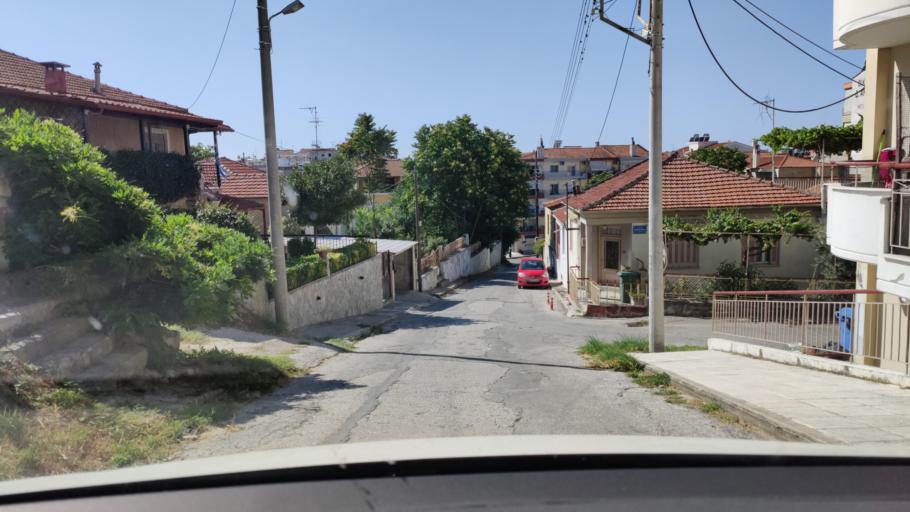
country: GR
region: Central Macedonia
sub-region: Nomos Serron
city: Serres
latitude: 41.0889
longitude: 23.5372
